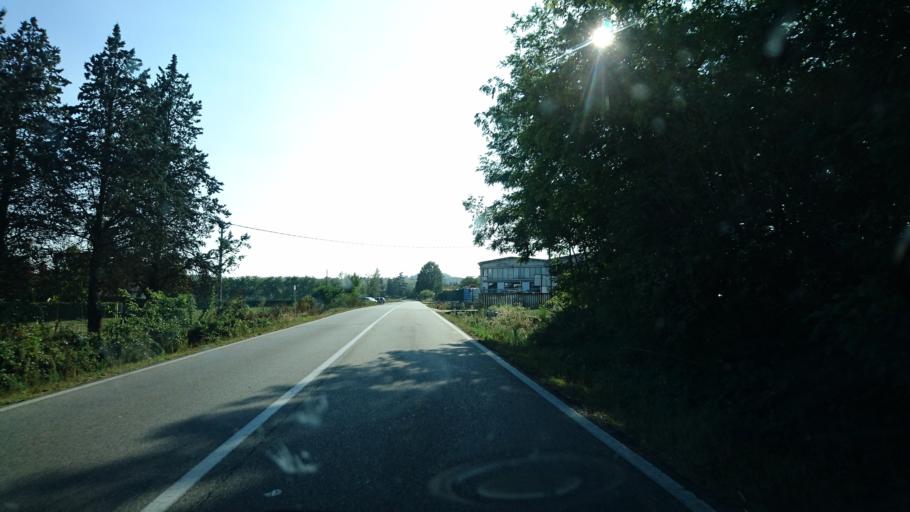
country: IT
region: Piedmont
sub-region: Provincia di Alessandria
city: Cassine
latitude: 44.7662
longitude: 8.5302
